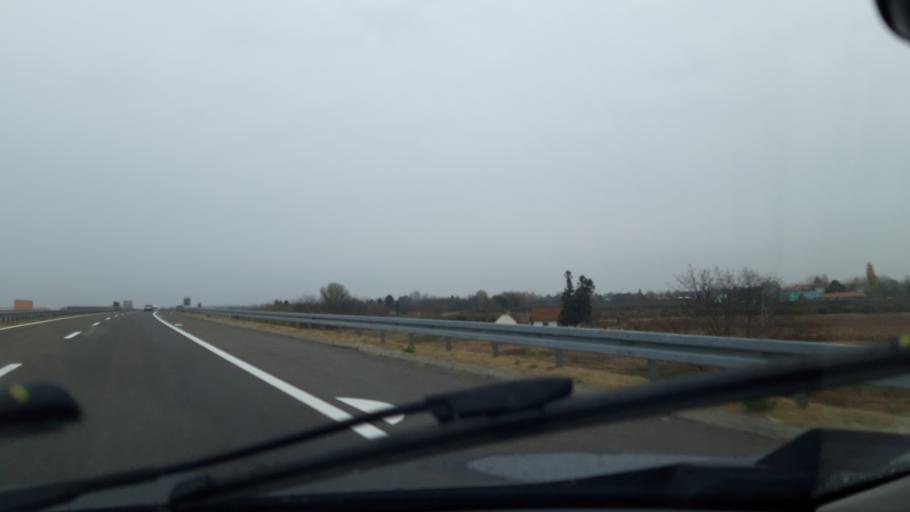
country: HU
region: Csongrad
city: Asotthalom
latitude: 46.1104
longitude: 19.7971
